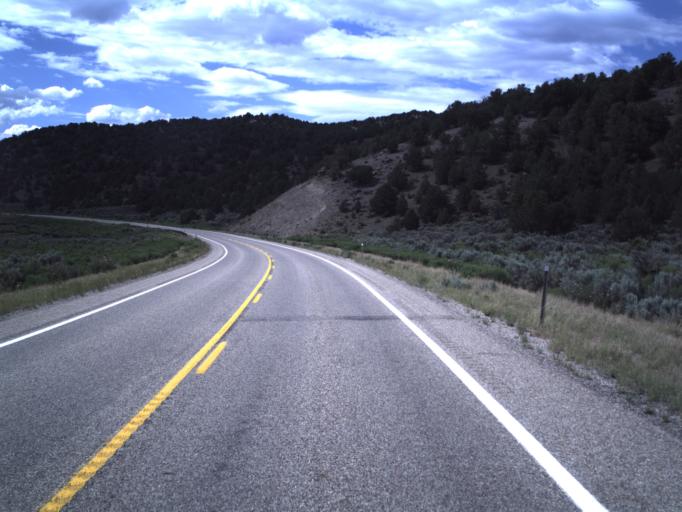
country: US
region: Utah
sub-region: Garfield County
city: Panguitch
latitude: 37.9828
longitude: -112.4869
